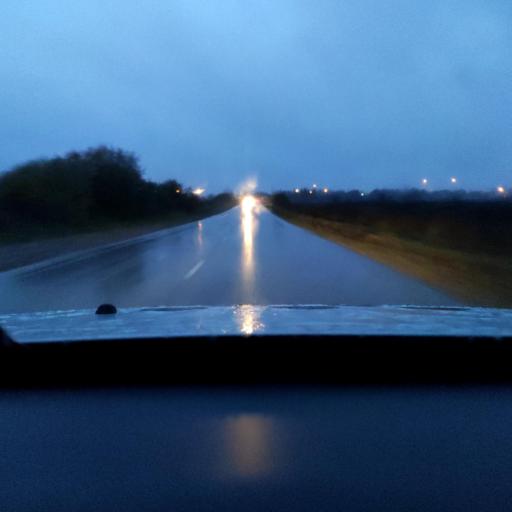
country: RU
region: Perm
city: Kondratovo
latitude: 58.0024
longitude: 56.0653
